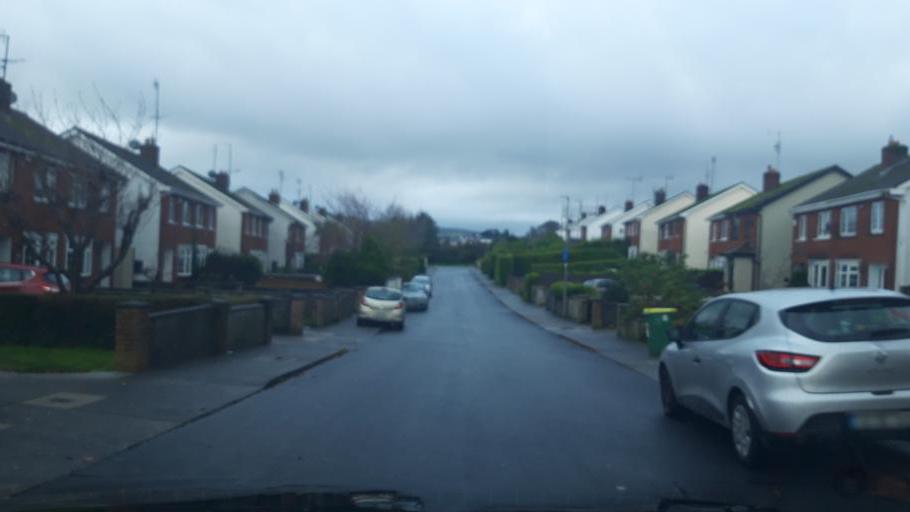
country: IE
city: Newtownmountkennedy
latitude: 53.0936
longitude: -6.1154
